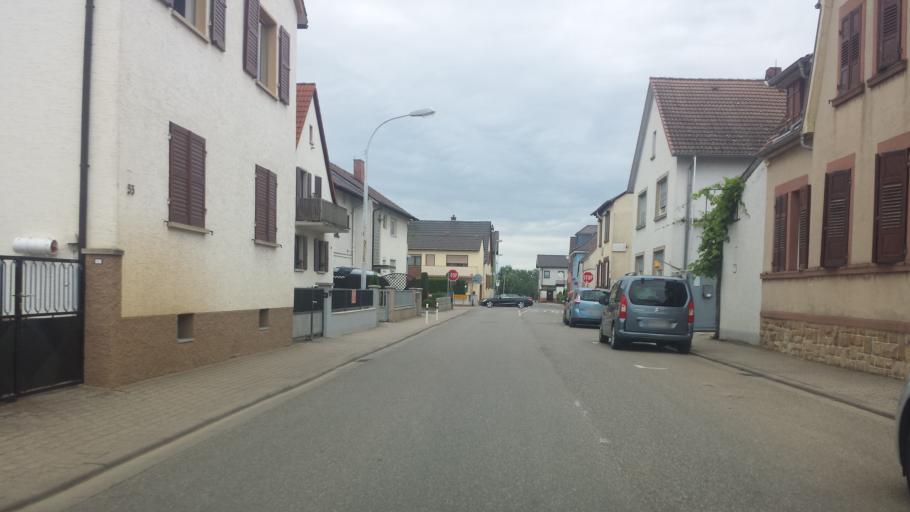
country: DE
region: Rheinland-Pfalz
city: Meckenheim
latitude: 49.4072
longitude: 8.2439
